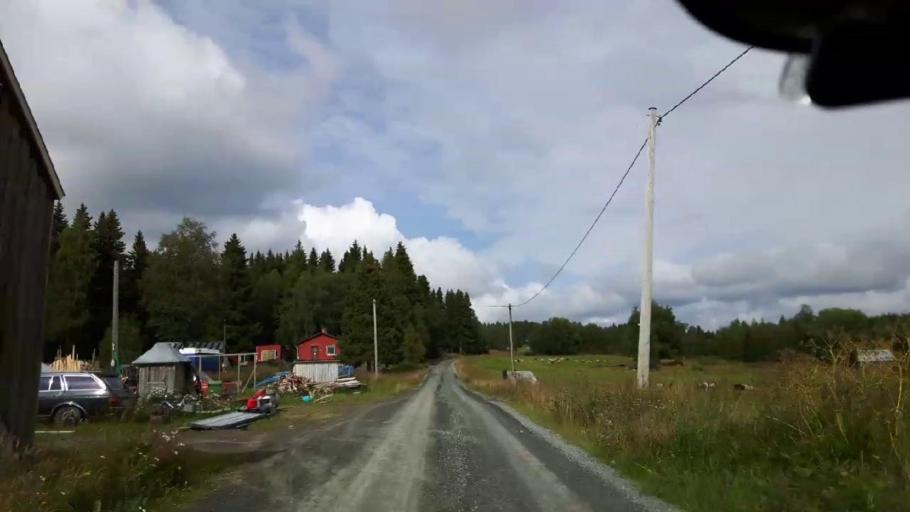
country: SE
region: Jaemtland
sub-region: Krokoms Kommun
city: Valla
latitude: 63.5682
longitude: 13.9171
